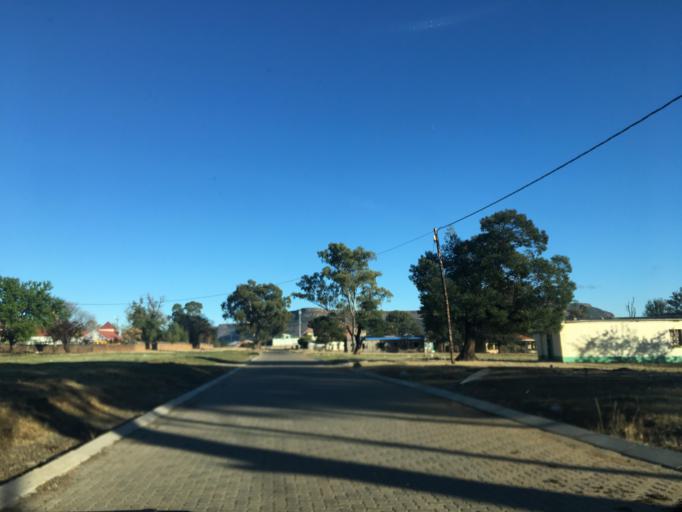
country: ZA
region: Eastern Cape
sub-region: Chris Hani District Municipality
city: Cala
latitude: -31.5259
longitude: 27.7016
